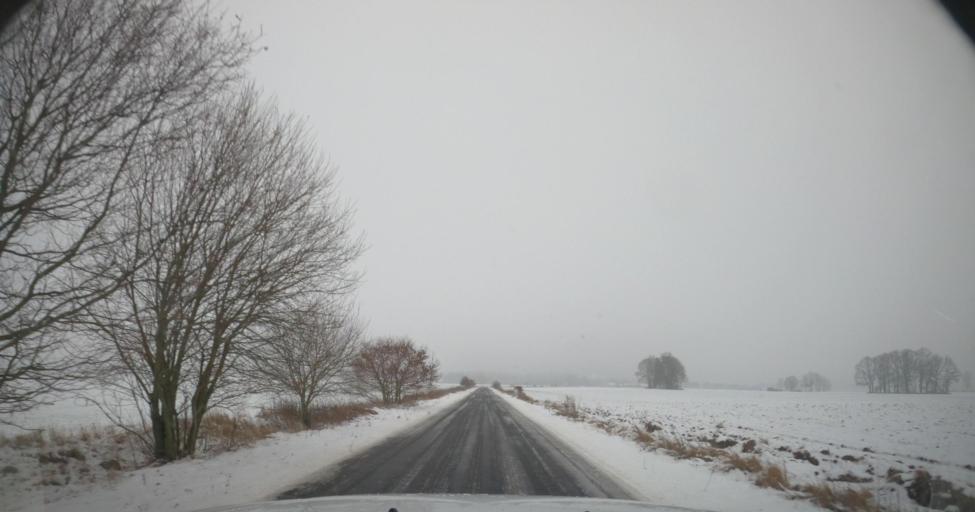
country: PL
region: West Pomeranian Voivodeship
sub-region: Powiat gryficki
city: Brojce
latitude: 53.8880
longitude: 15.3888
